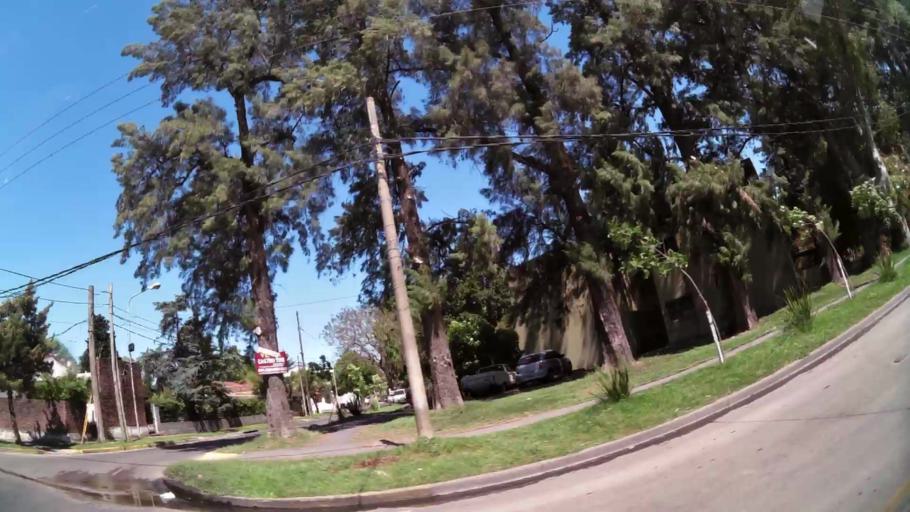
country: AR
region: Buenos Aires
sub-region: Partido de Tigre
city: Tigre
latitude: -34.4870
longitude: -58.6452
